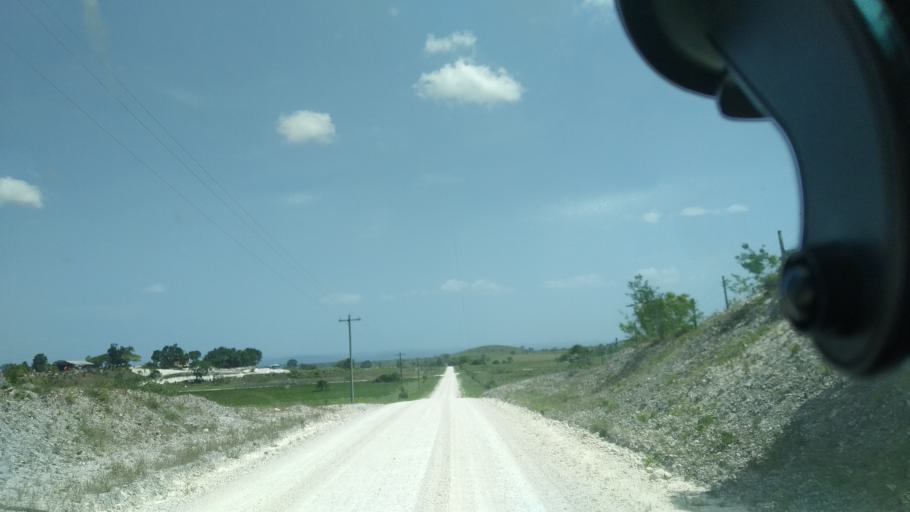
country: BZ
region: Cayo
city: San Ignacio
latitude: 17.3040
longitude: -89.0480
